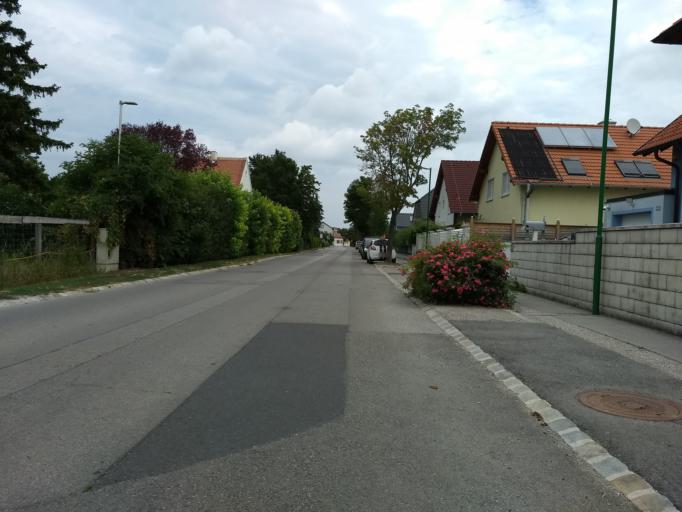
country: AT
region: Lower Austria
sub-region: Politischer Bezirk Modling
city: Guntramsdorf
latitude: 48.0419
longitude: 16.3113
